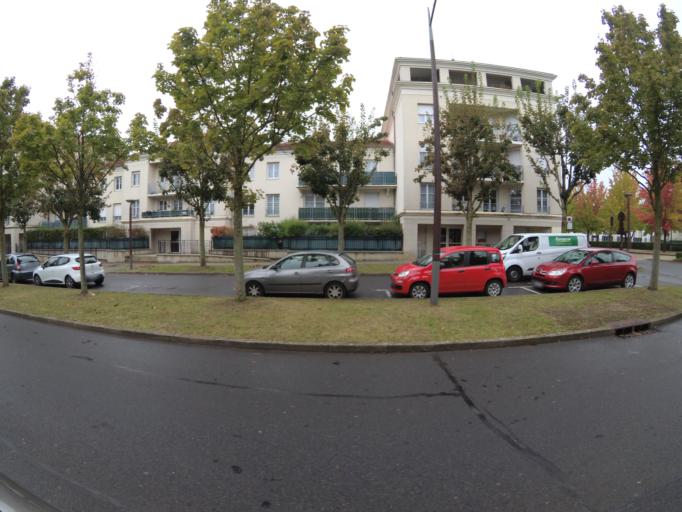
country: FR
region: Ile-de-France
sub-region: Departement de Seine-et-Marne
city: Conches-sur-Gondoire
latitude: 48.8399
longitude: 2.7213
